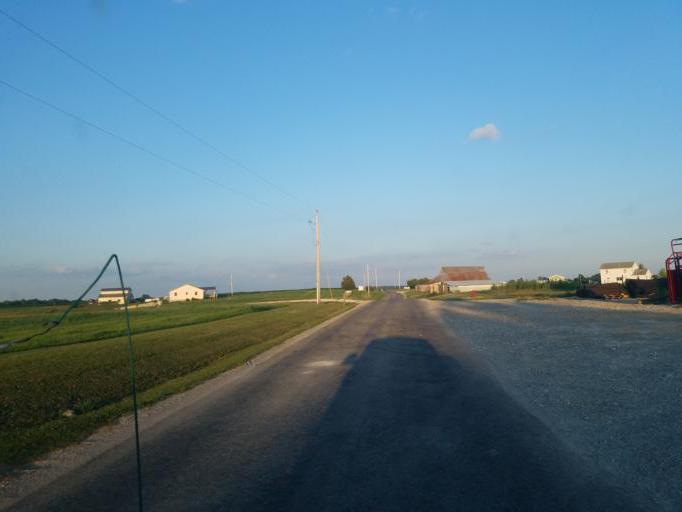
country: US
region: Illinois
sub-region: Jackson County
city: Murphysboro
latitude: 37.6749
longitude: -89.3072
